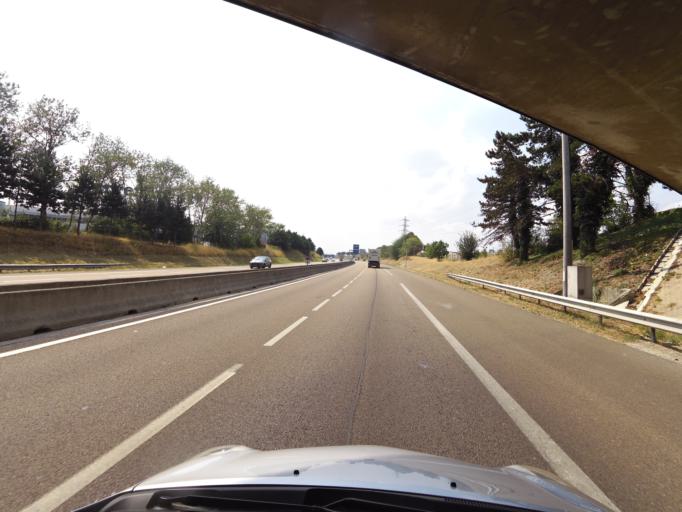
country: FR
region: Champagne-Ardenne
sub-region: Departement de la Marne
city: Tinqueux
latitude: 49.2562
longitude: 3.9820
